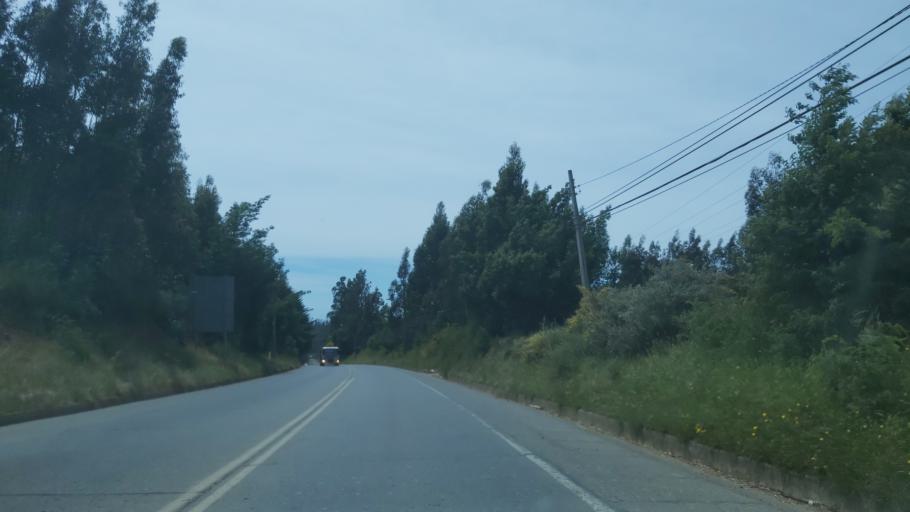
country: CL
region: Maule
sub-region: Provincia de Talca
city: Constitucion
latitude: -35.3589
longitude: -72.4062
